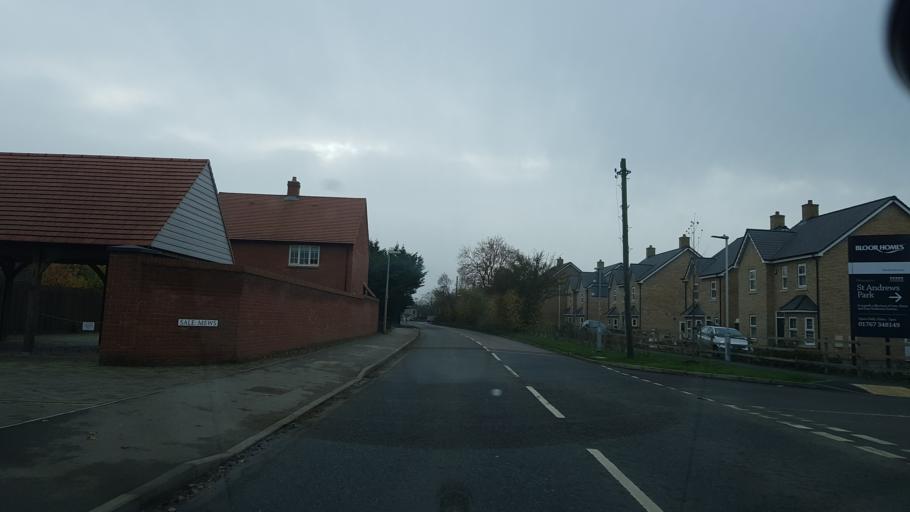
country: GB
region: England
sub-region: Central Bedfordshire
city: Biggleswade
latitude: 52.0971
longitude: -0.2502
